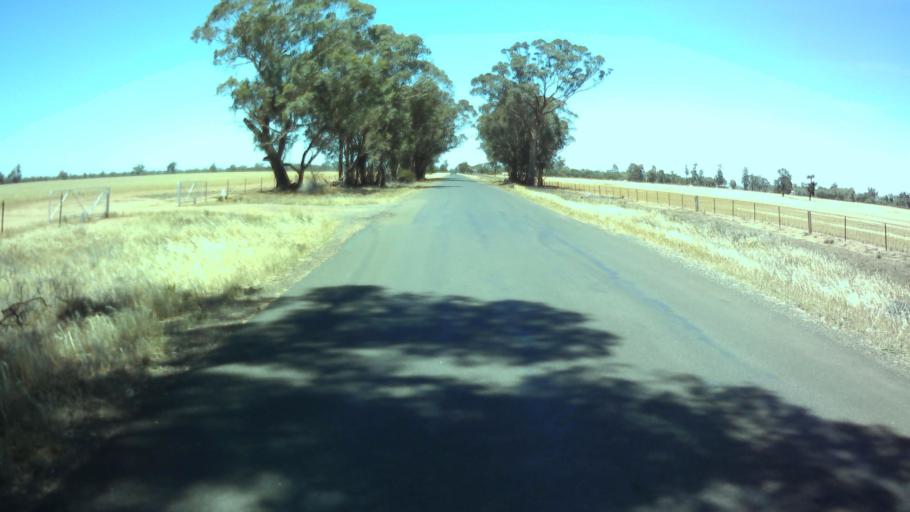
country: AU
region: New South Wales
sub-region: Weddin
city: Grenfell
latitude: -34.0240
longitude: 147.7920
